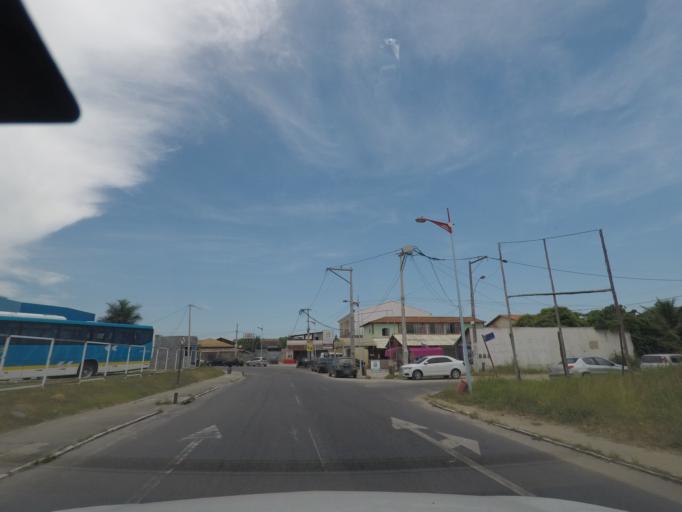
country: BR
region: Rio de Janeiro
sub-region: Marica
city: Marica
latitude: -22.9619
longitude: -42.9625
